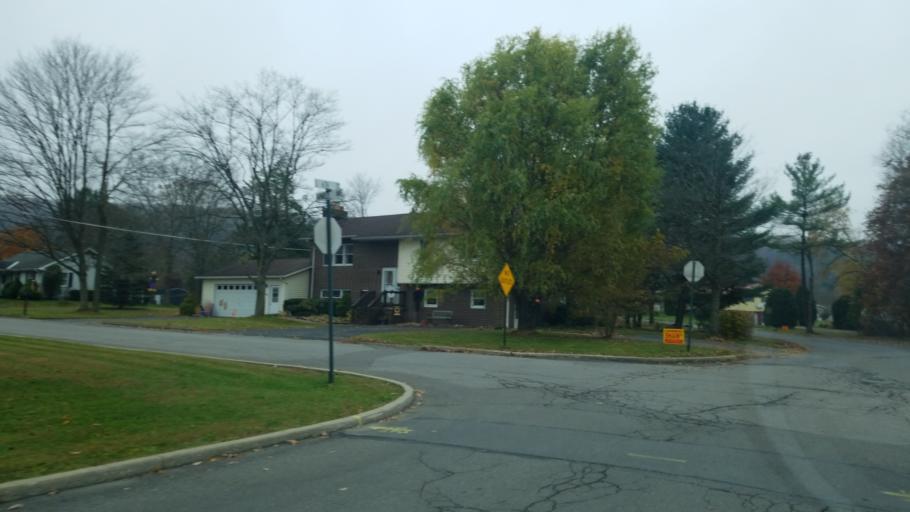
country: US
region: Pennsylvania
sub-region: Clearfield County
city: Clearfield
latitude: 41.0098
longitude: -78.4385
